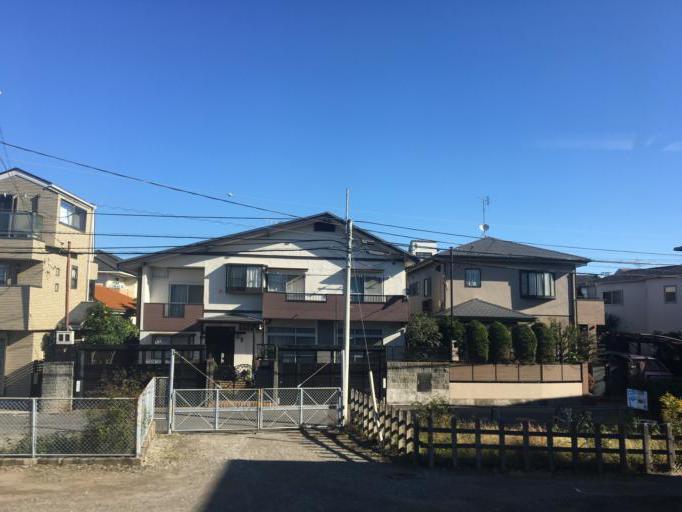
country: JP
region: Chiba
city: Funabashi
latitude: 35.7052
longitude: 139.9732
